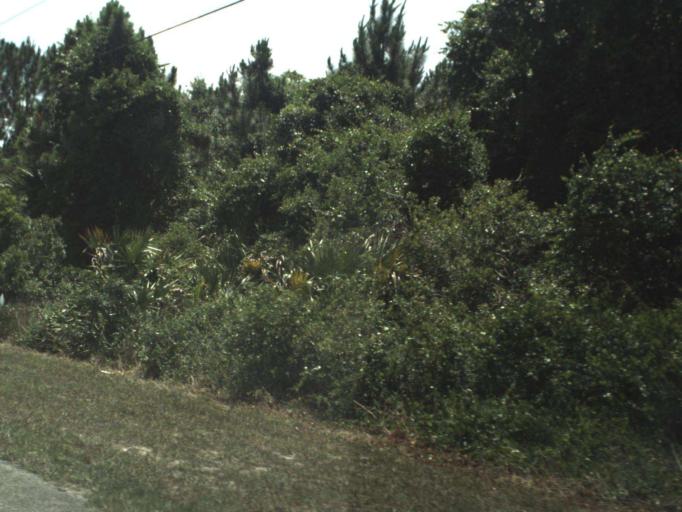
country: US
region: Florida
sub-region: Volusia County
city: Edgewater
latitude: 28.9347
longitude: -80.8789
